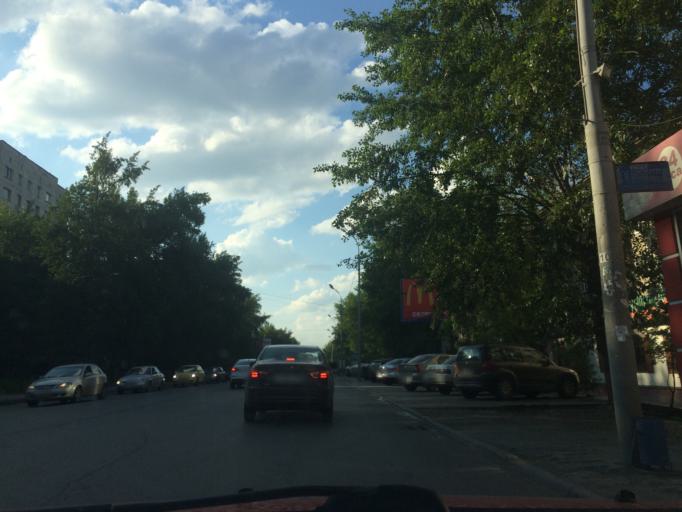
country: RU
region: Sverdlovsk
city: Yekaterinburg
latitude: 56.8269
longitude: 60.6377
